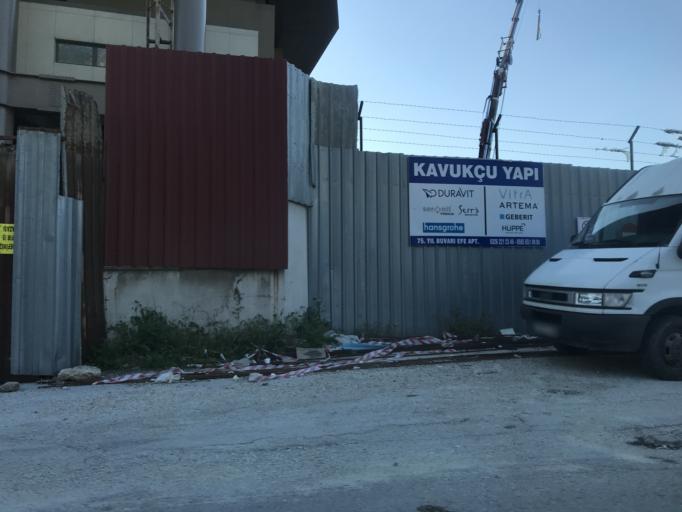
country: TR
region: Hatay
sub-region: Antakya Ilcesi
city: Antakya
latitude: 36.2111
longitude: 36.1747
